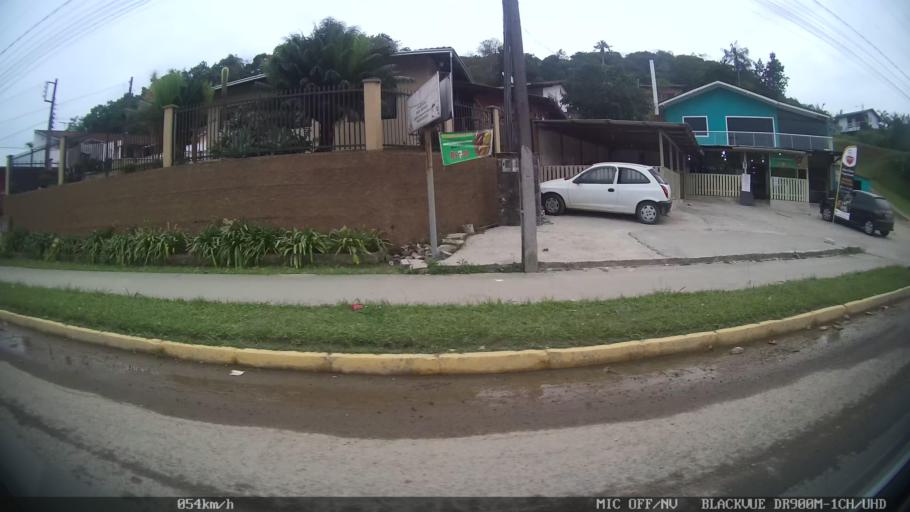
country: BR
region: Santa Catarina
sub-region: Joinville
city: Joinville
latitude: -26.3688
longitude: -48.8337
